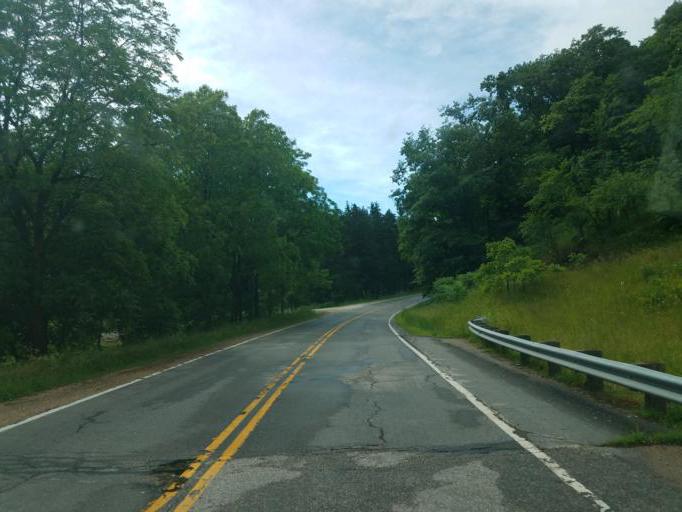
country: US
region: Wisconsin
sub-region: Vernon County
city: Hillsboro
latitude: 43.6609
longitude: -90.4427
